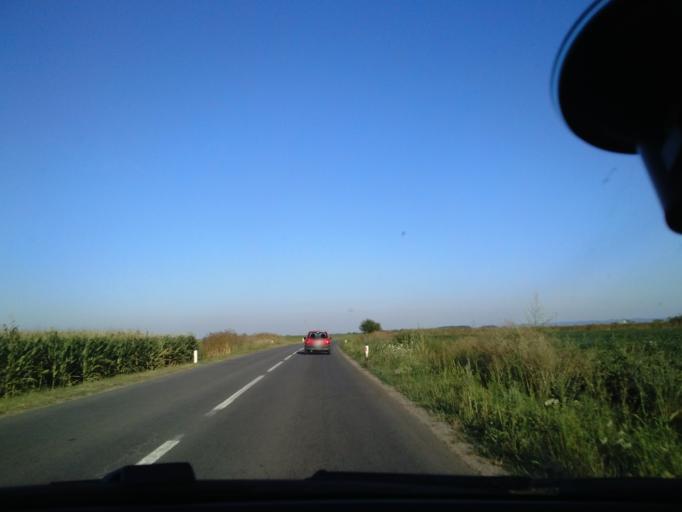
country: RS
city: Maglic
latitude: 45.3852
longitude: 19.5044
